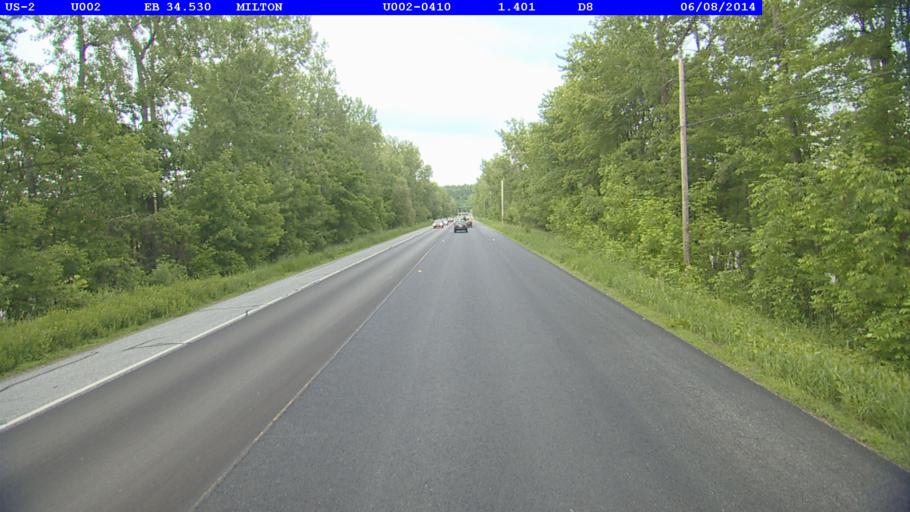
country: US
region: Vermont
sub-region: Chittenden County
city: Colchester
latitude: 44.6246
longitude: -73.2296
